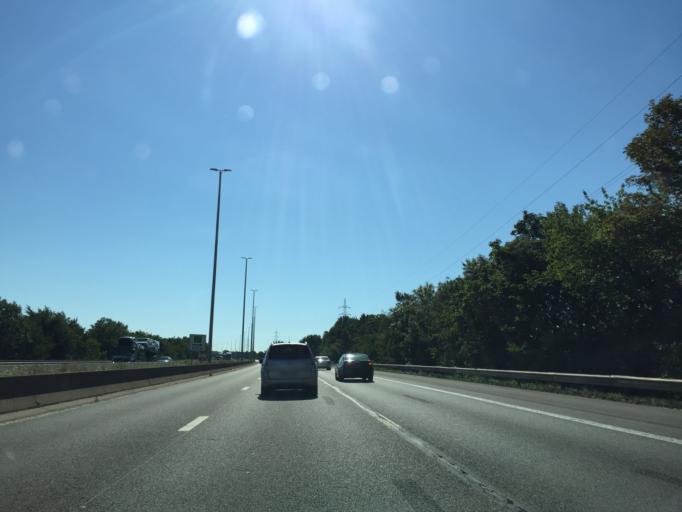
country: BE
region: Wallonia
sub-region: Province de Liege
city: Soumagne
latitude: 50.6376
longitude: 5.7395
